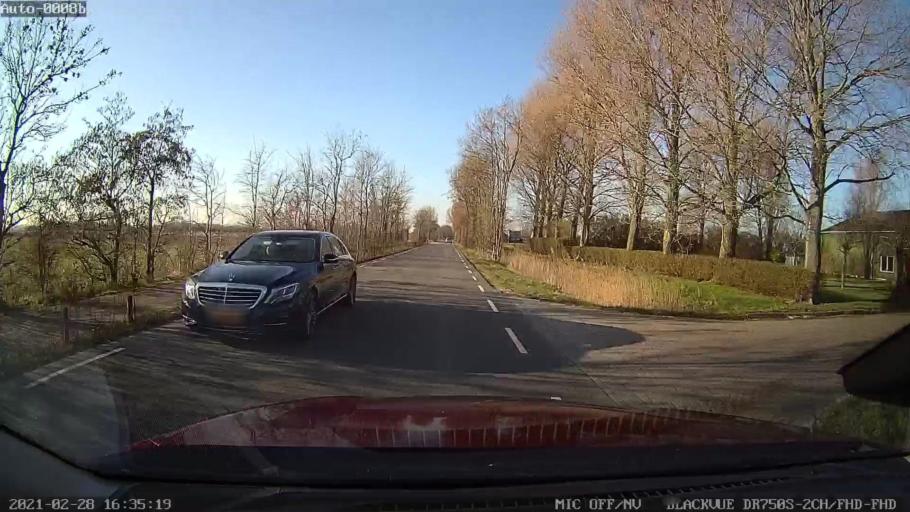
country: NL
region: Zeeland
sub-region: Gemeente Middelburg
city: Middelburg
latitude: 51.5102
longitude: 3.5813
